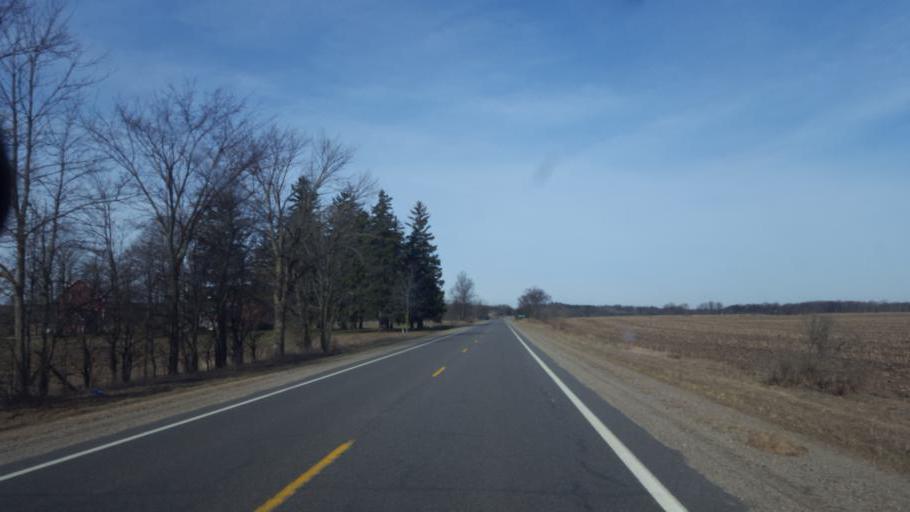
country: US
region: Michigan
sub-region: Montcalm County
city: Lakeview
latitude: 43.4315
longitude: -85.3165
